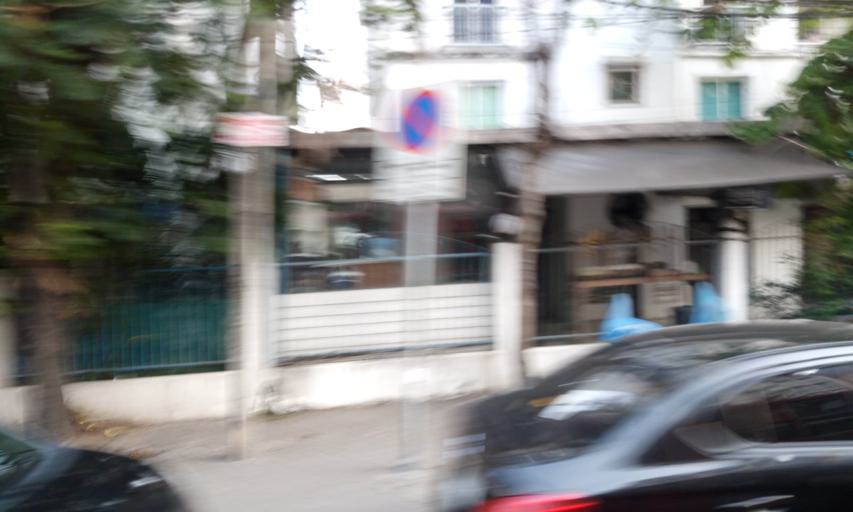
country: TH
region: Bangkok
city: Lat Phrao
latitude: 13.8240
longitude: 100.6153
